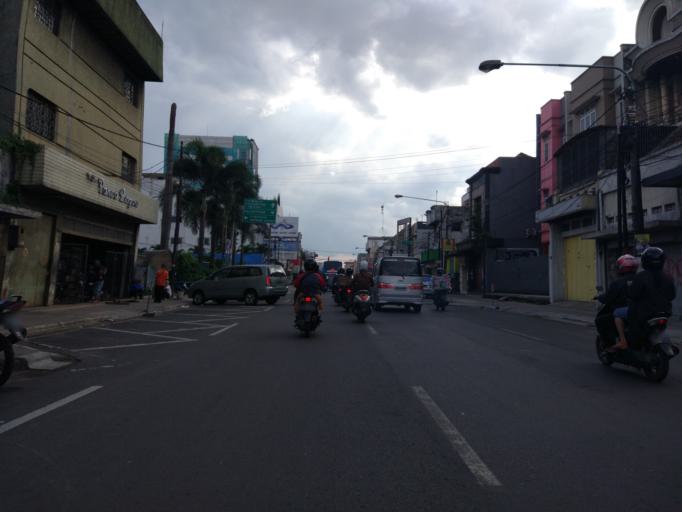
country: ID
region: West Java
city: Bandung
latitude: -6.9197
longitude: 107.5944
